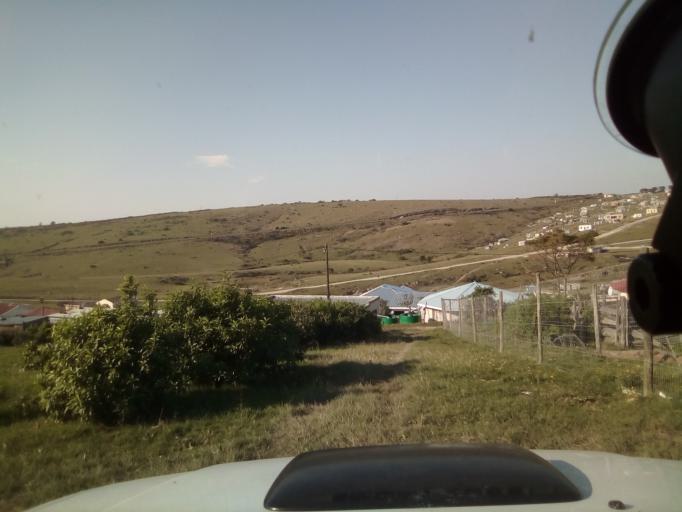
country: ZA
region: Eastern Cape
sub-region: Buffalo City Metropolitan Municipality
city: East London
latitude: -32.8471
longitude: 27.9898
